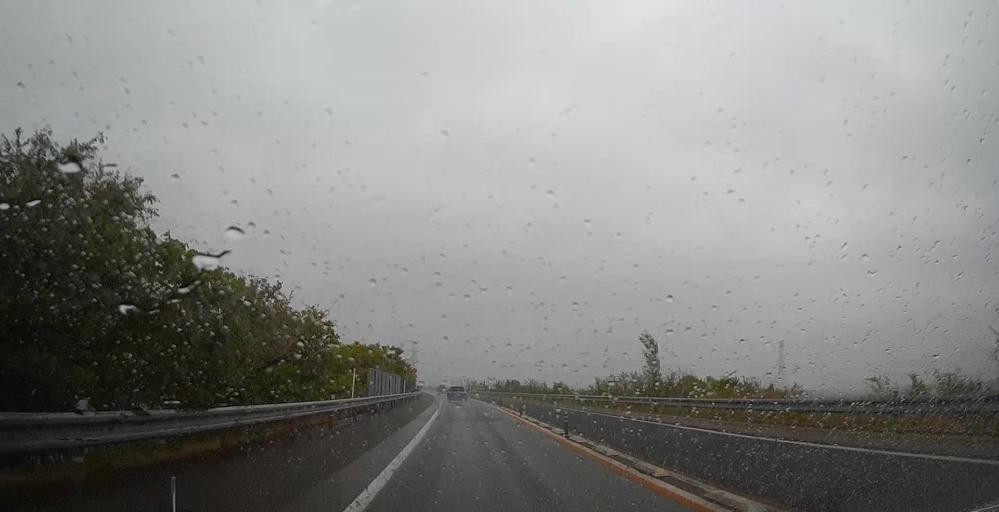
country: JP
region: Niigata
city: Shibata
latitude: 37.9447
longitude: 139.2709
